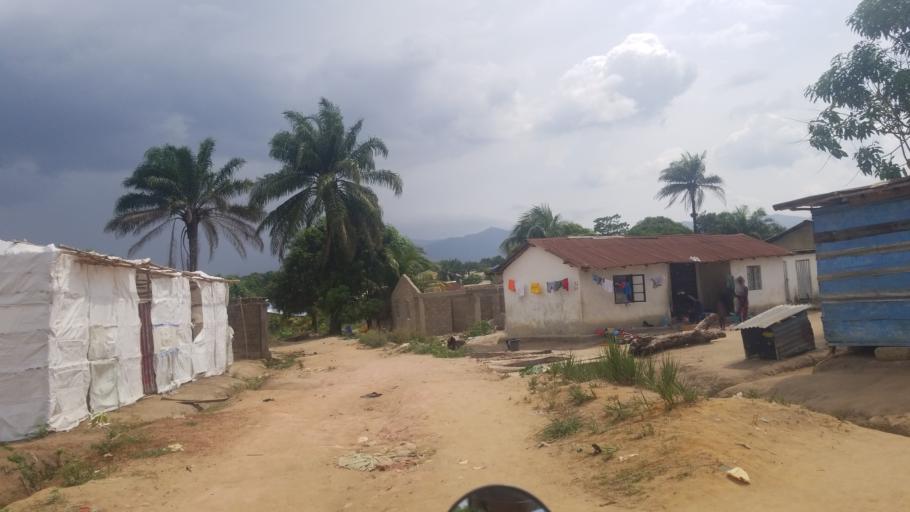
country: SL
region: Western Area
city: Waterloo
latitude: 8.3239
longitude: -13.0419
